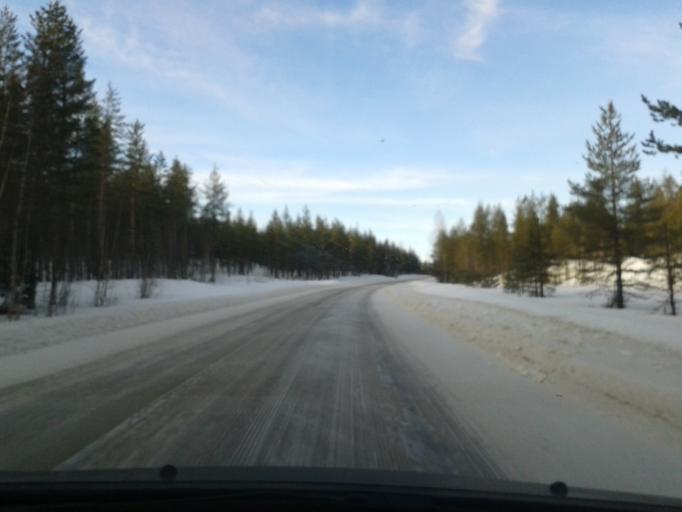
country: SE
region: Vaesternorrland
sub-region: OErnskoeldsviks Kommun
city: Bredbyn
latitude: 63.6355
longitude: 17.9054
